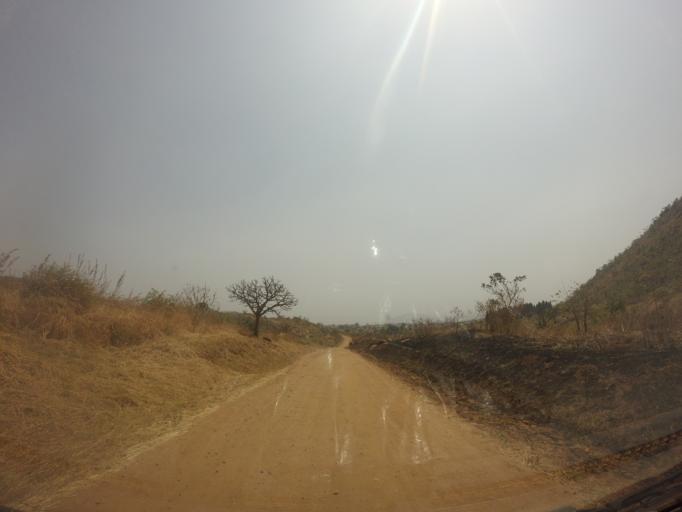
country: UG
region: Northern Region
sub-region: Arua District
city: Arua
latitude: 2.9243
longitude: 30.9897
